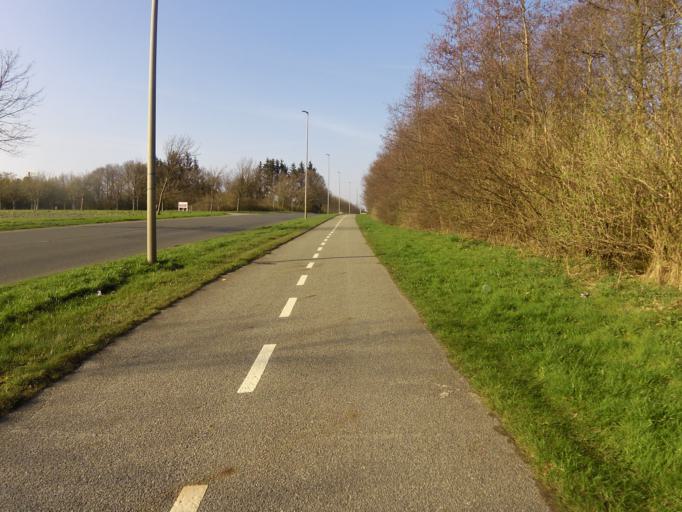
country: DK
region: South Denmark
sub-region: Vejen Kommune
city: Vejen
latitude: 55.4831
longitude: 9.1250
